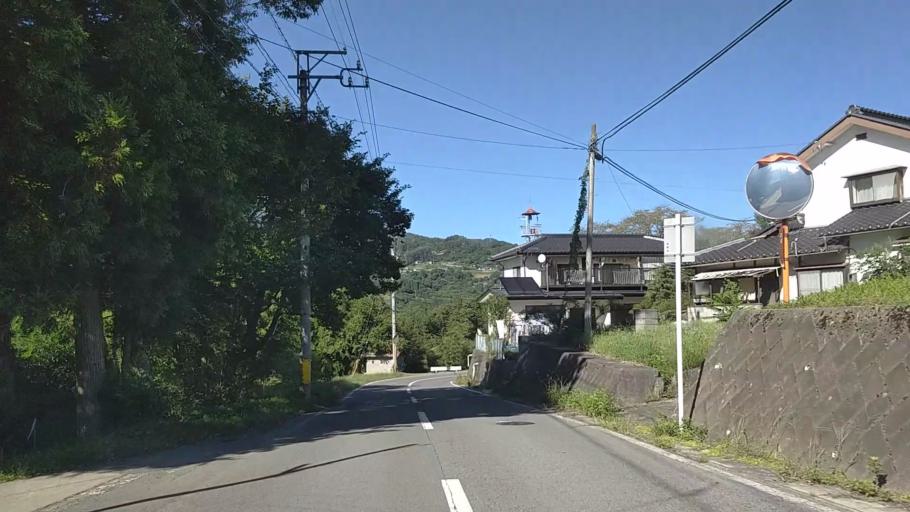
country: JP
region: Nagano
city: Nagano-shi
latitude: 36.6116
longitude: 138.0886
